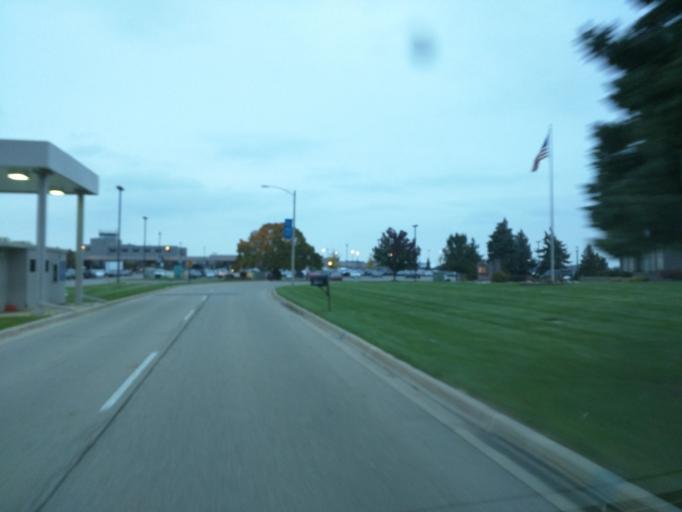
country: US
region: Michigan
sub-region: Ingham County
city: Edgemont Park
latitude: 42.7724
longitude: -84.5888
